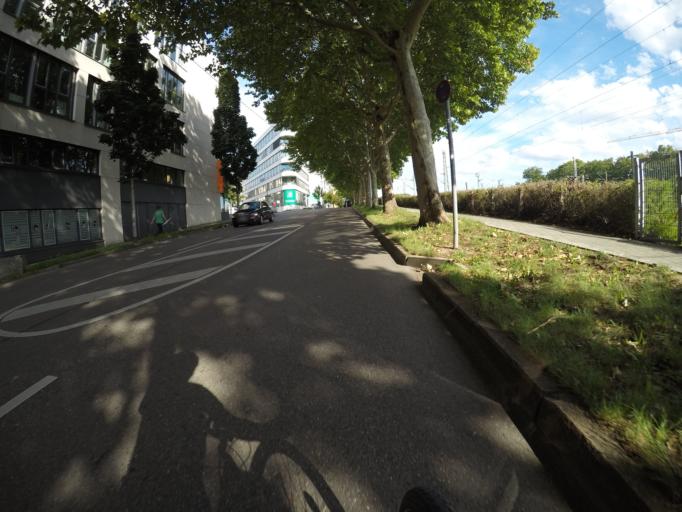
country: DE
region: Baden-Wuerttemberg
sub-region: Regierungsbezirk Stuttgart
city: Stuttgart-Ost
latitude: 48.8007
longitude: 9.2224
